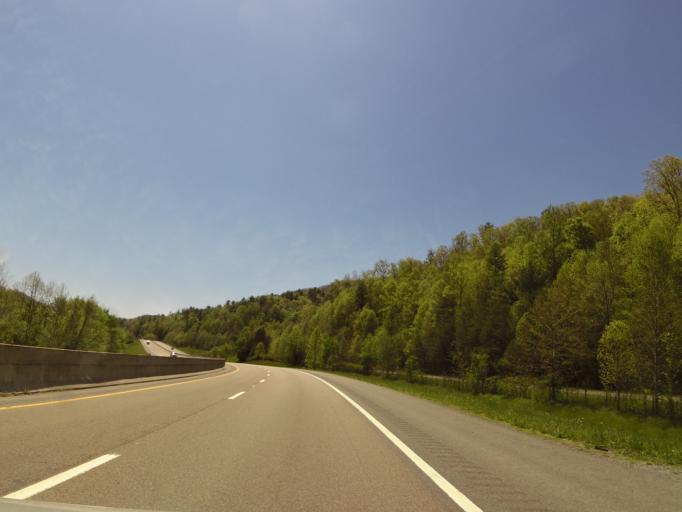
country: US
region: Tennessee
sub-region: Unicoi County
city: Banner Hill
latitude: 36.0974
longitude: -82.4777
